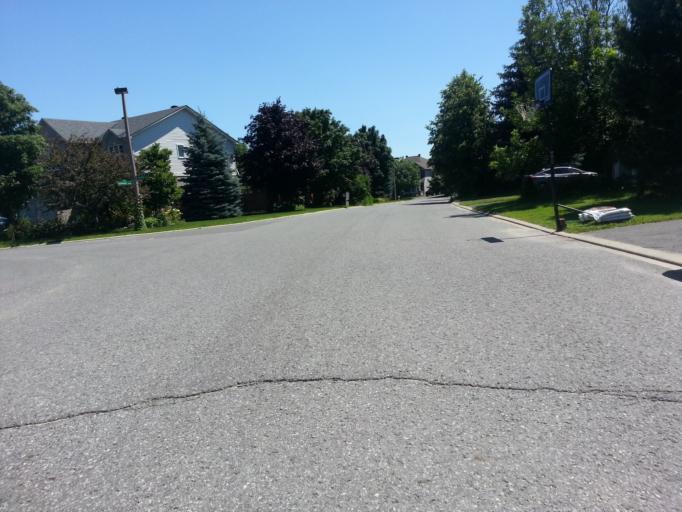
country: CA
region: Ontario
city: Bells Corners
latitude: 45.3249
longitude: -75.9220
